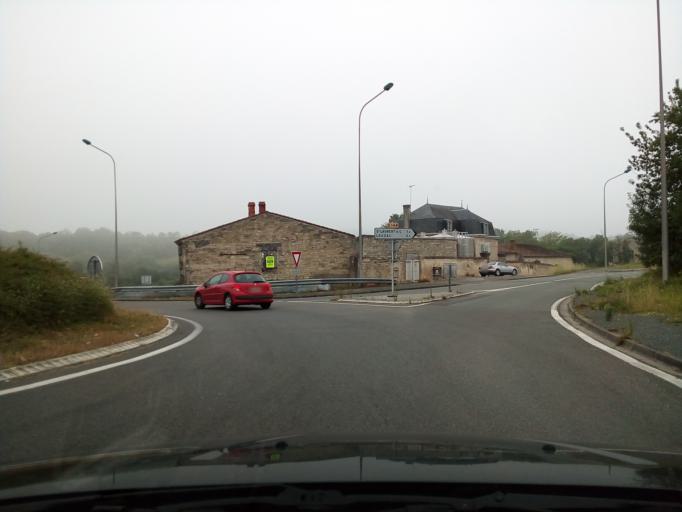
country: FR
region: Poitou-Charentes
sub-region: Departement de la Charente-Maritime
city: Cherac
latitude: 45.6882
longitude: -0.3969
